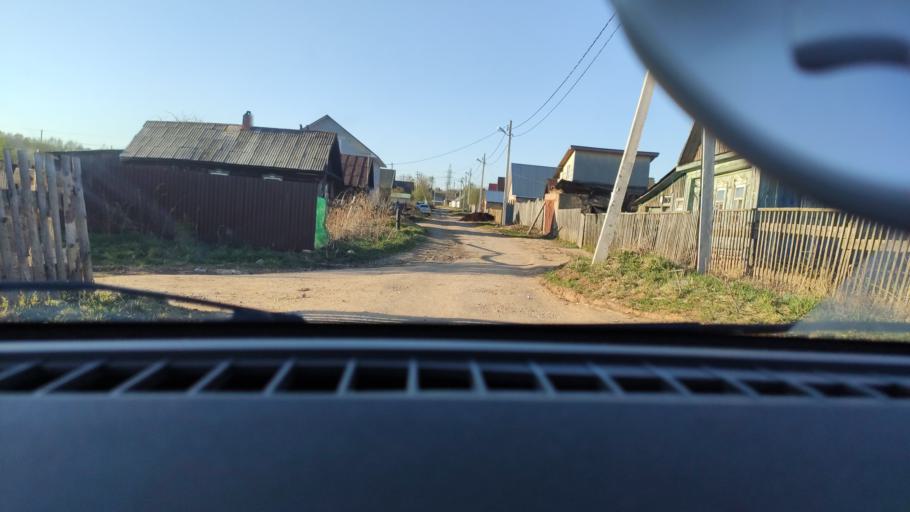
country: RU
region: Perm
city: Perm
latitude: 58.0359
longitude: 56.3994
